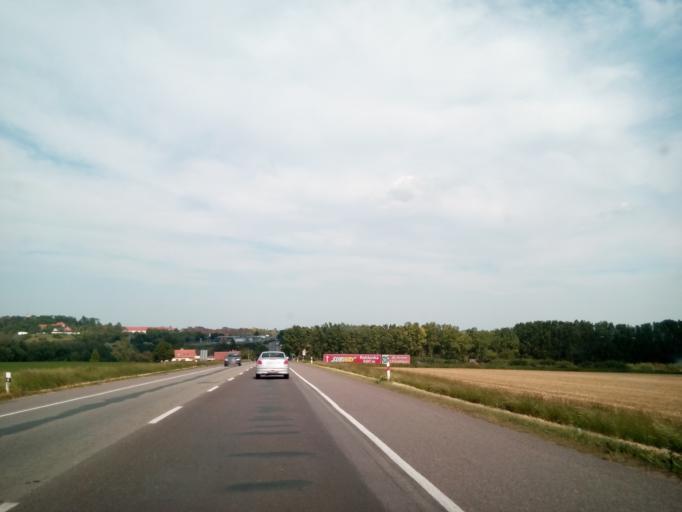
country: CZ
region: South Moravian
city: Tvarozna
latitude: 49.1834
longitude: 16.7479
